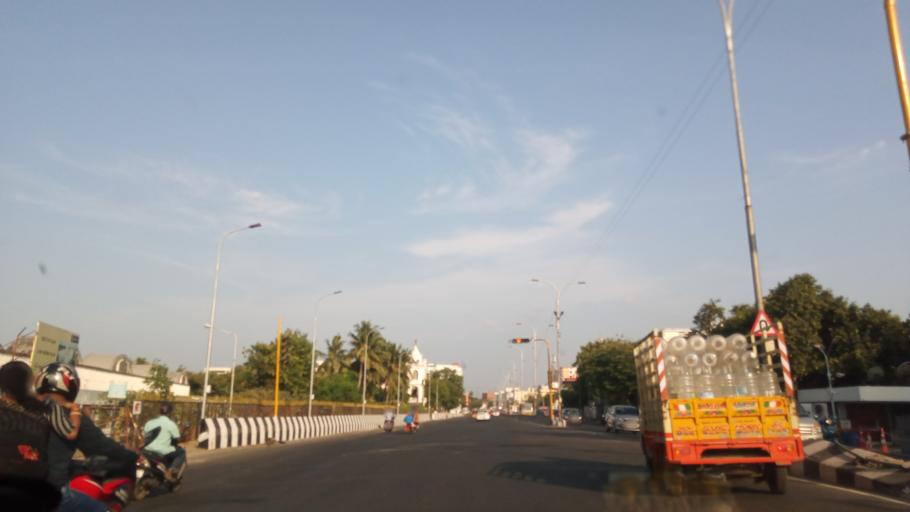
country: IN
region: Tamil Nadu
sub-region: Kancheepuram
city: Manappakkam
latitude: 13.0238
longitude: 80.1788
